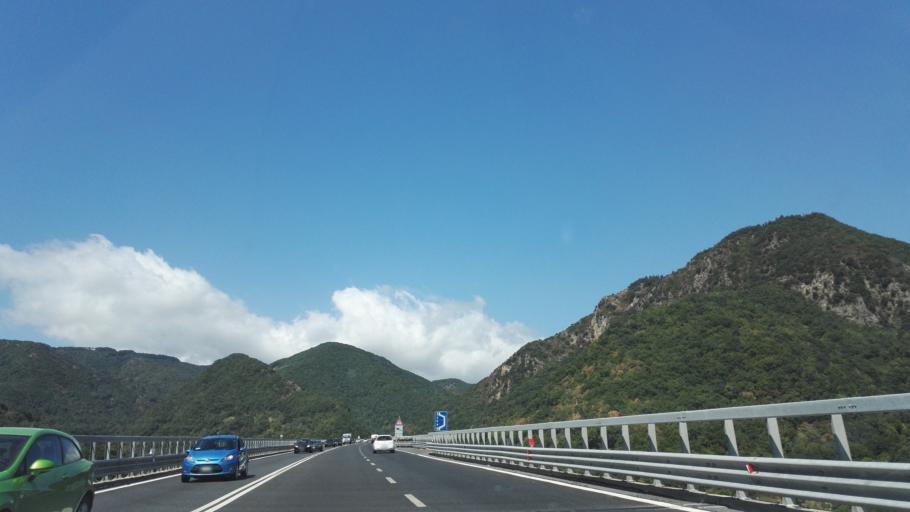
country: IT
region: Calabria
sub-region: Provincia di Reggio Calabria
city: Mammola
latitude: 38.3595
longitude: 16.2090
